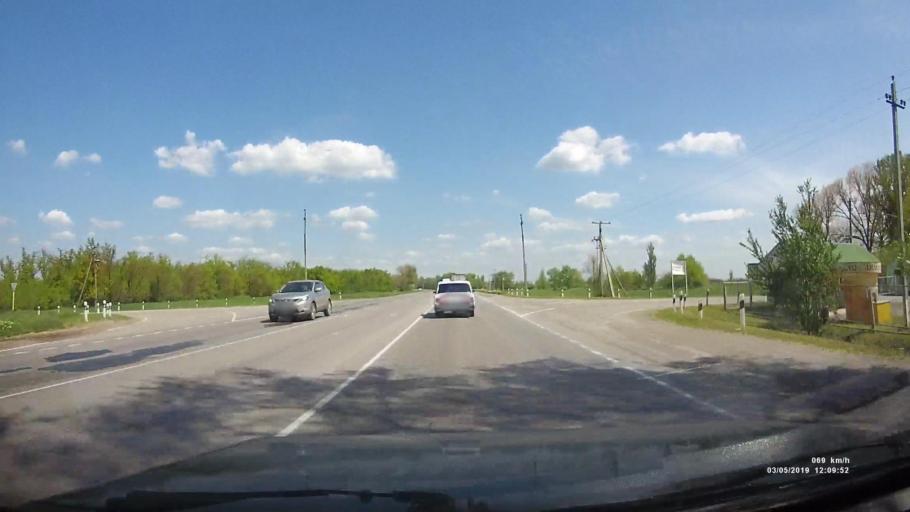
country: RU
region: Rostov
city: Bagayevskaya
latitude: 47.2969
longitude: 40.5221
